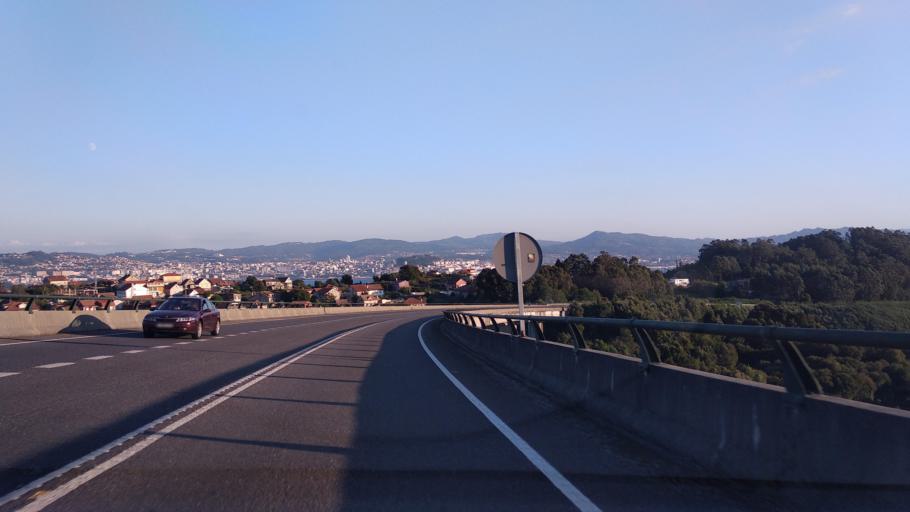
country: ES
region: Galicia
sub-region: Provincia de Pontevedra
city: Moana
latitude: 42.2828
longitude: -8.7530
